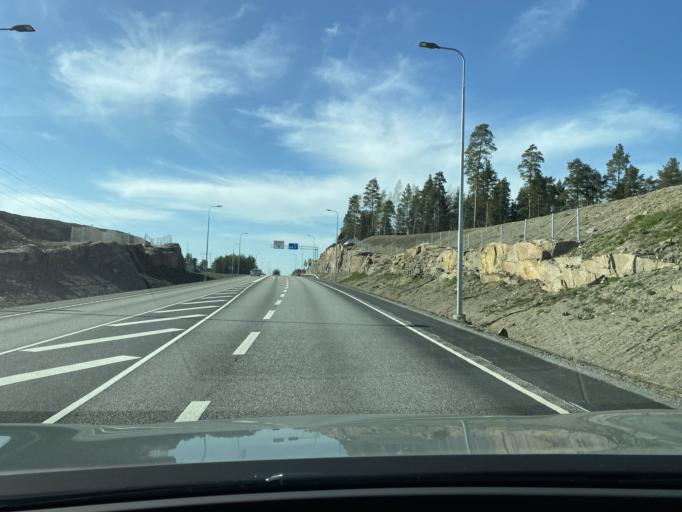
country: FI
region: Uusimaa
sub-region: Helsinki
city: Nurmijaervi
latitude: 60.4033
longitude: 24.7660
